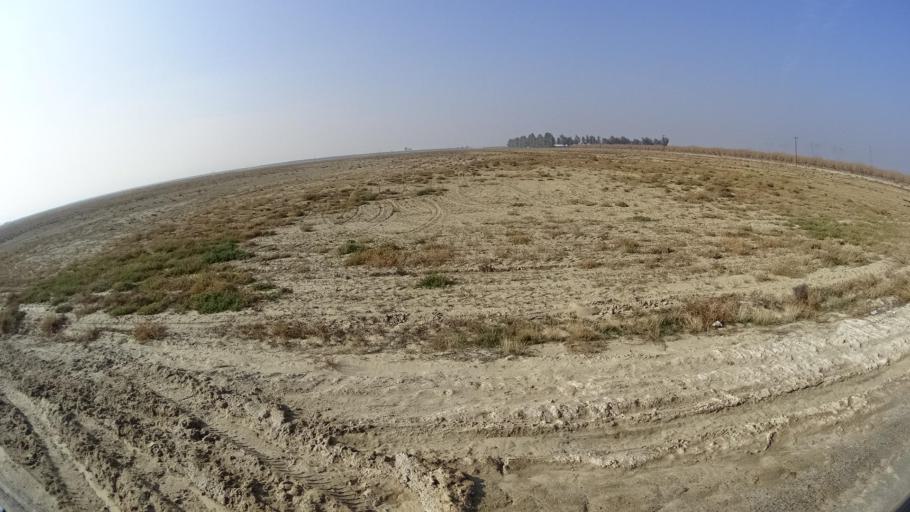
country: US
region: California
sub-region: Kern County
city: Buttonwillow
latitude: 35.3538
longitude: -119.3591
